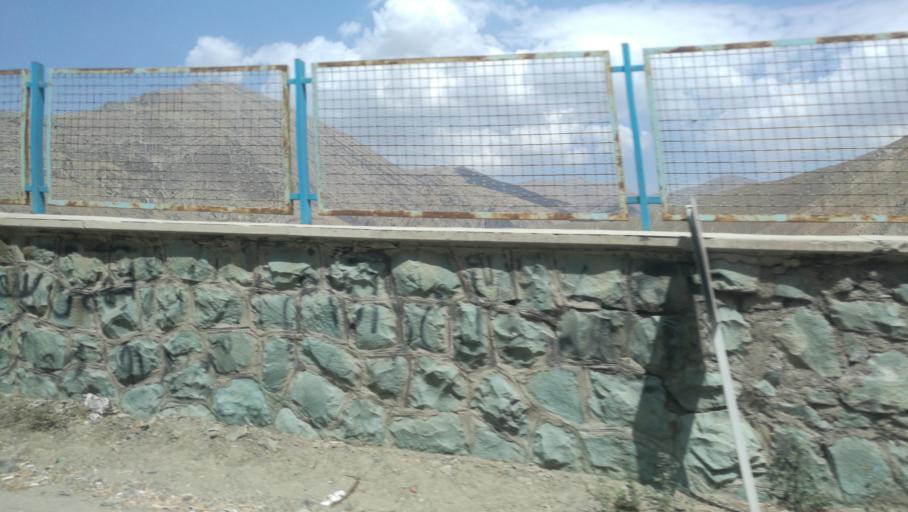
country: IR
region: Alborz
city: Karaj
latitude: 35.9638
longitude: 51.0935
